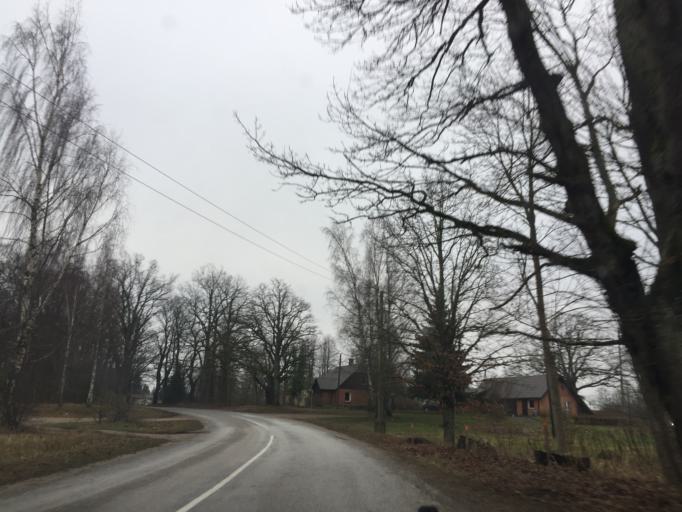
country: LV
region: Limbazu Rajons
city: Limbazi
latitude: 57.5198
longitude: 24.6863
